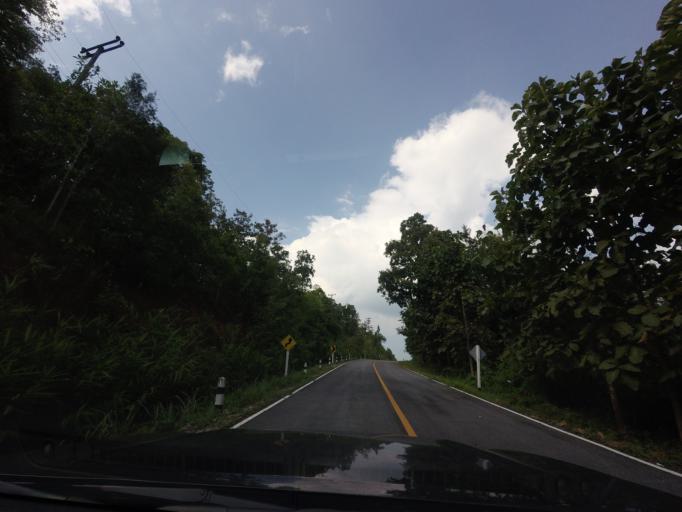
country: TH
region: Uttaradit
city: Ban Khok
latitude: 18.2262
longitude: 101.0325
